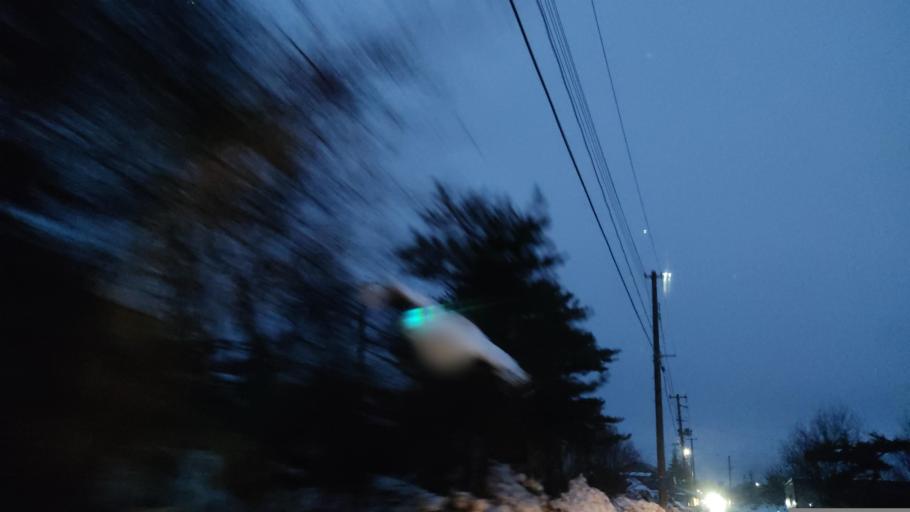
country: JP
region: Iwate
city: Morioka-shi
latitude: 39.6307
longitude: 141.1062
